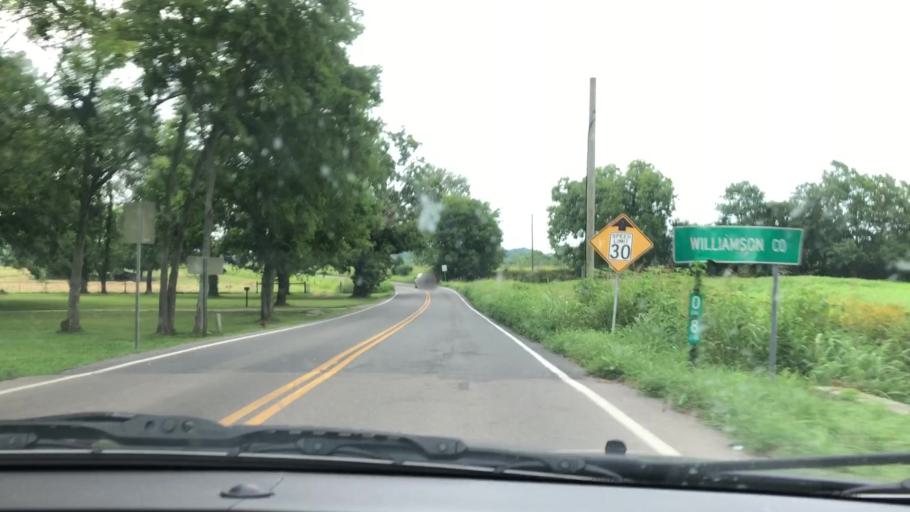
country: US
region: Tennessee
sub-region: Maury County
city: Spring Hill
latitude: 35.7805
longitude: -87.0037
